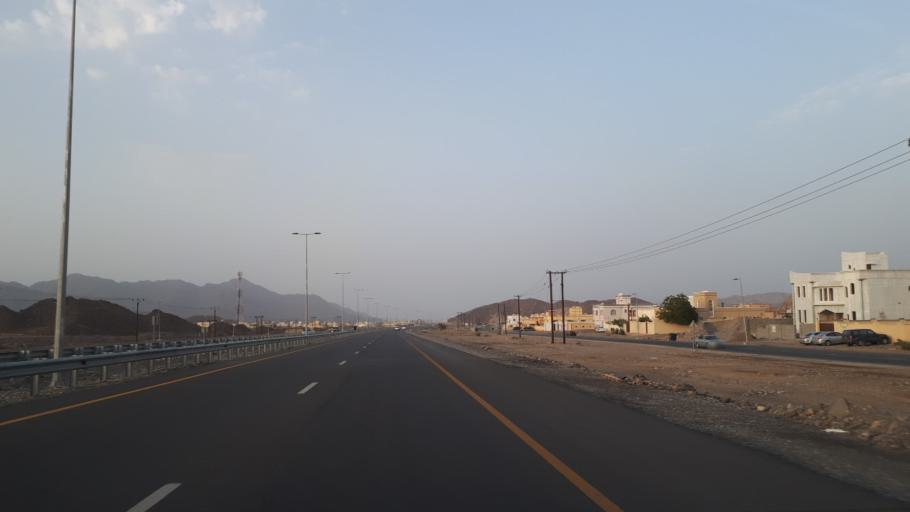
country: OM
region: Al Batinah
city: Rustaq
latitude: 23.4140
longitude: 57.3585
